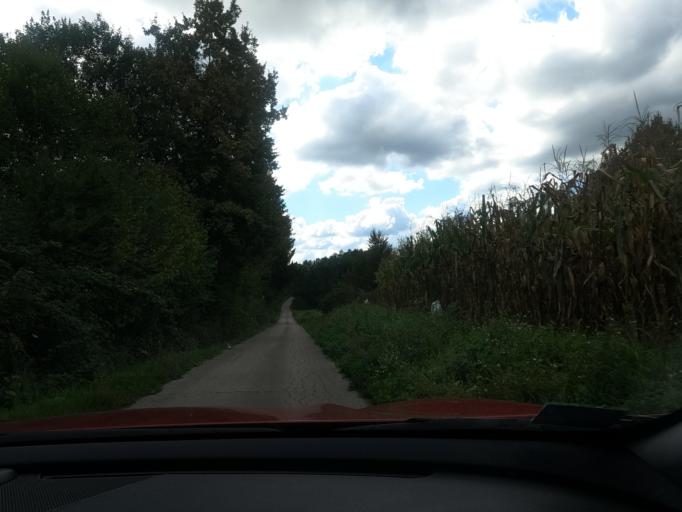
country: HR
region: Karlovacka
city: Vojnic
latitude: 45.2229
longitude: 15.7101
